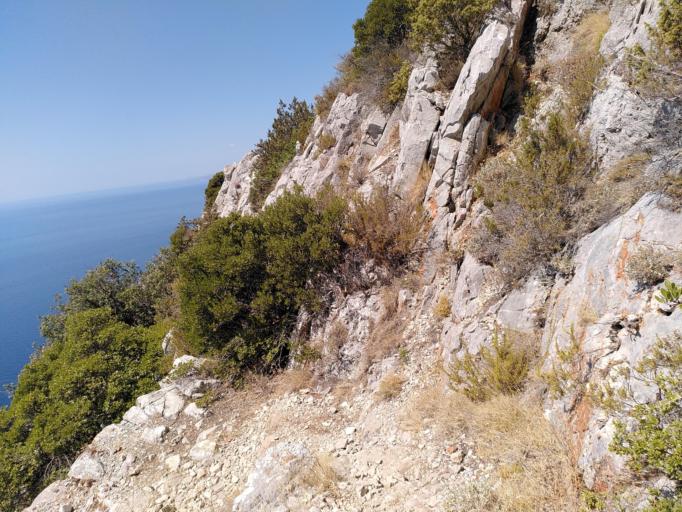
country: HR
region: Splitsko-Dalmatinska
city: Stari Grad
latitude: 43.1455
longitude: 16.5824
